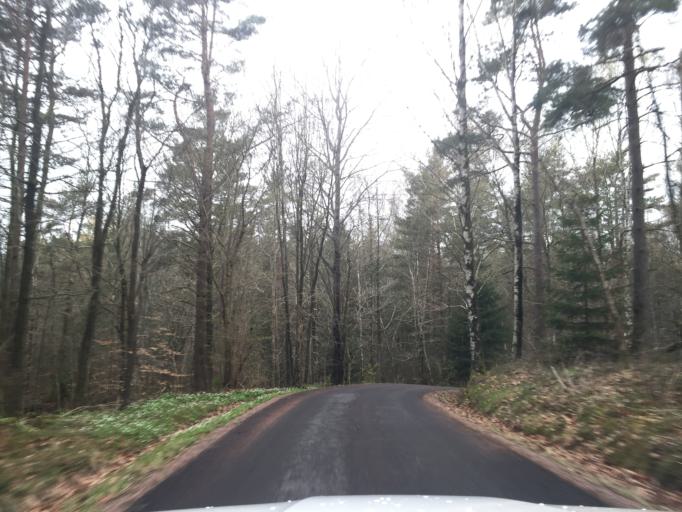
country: SE
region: Vaestra Goetaland
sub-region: Kungalvs Kommun
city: Kungalv
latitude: 57.8456
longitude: 11.9904
